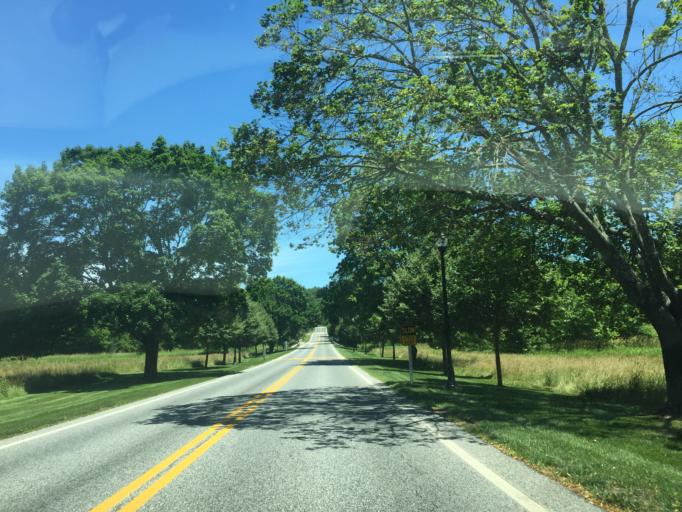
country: US
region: Maryland
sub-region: Baltimore County
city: Garrison
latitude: 39.3821
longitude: -76.7597
